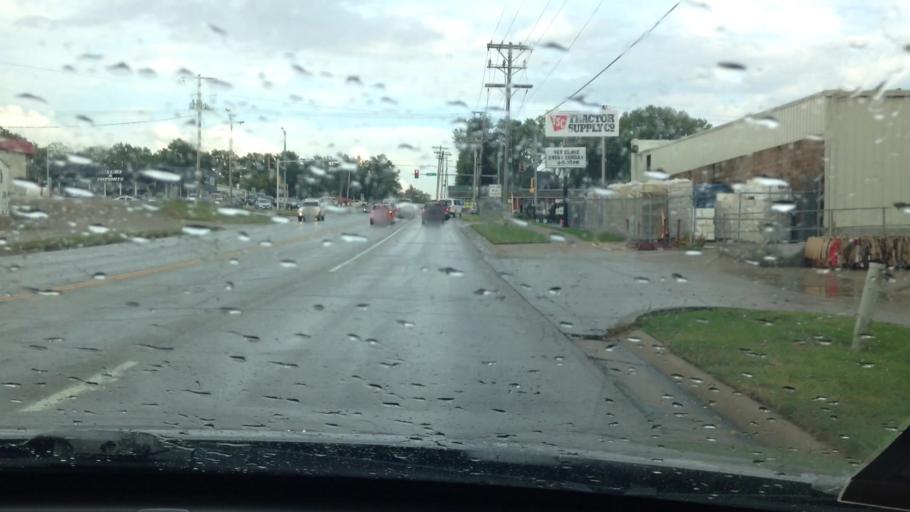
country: US
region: Kansas
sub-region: Leavenworth County
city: Lansing
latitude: 39.2669
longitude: -94.9013
